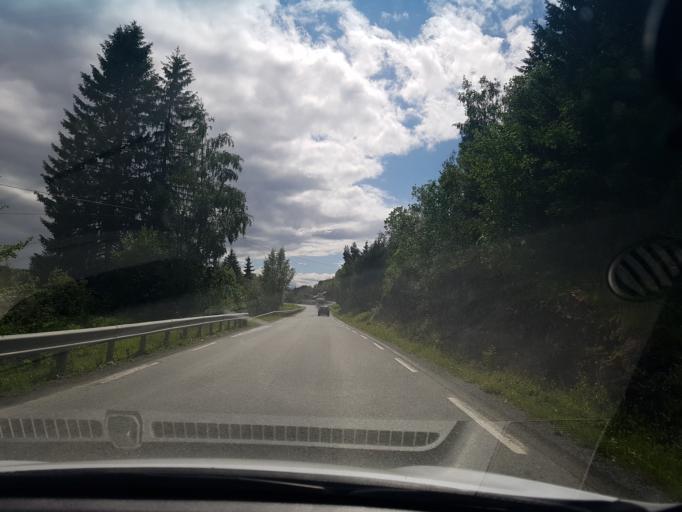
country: NO
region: Nord-Trondelag
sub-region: Frosta
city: Frosta
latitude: 63.6063
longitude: 10.8780
